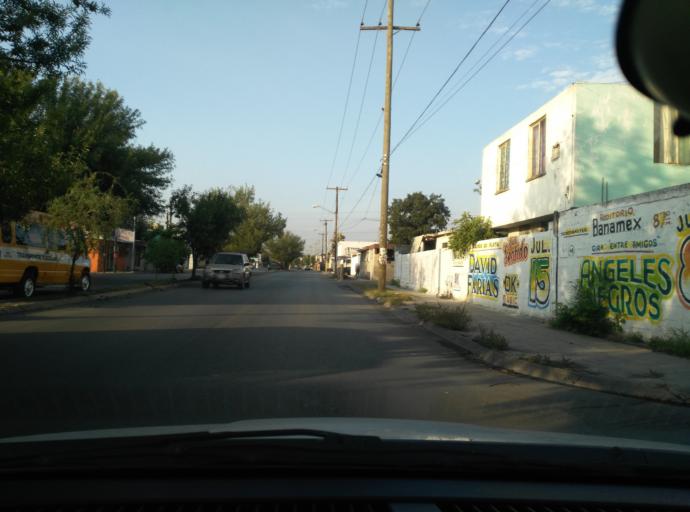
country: MX
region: Nuevo Leon
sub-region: San Nicolas de los Garza
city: San Nicolas de los Garza
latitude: 25.7657
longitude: -100.2494
